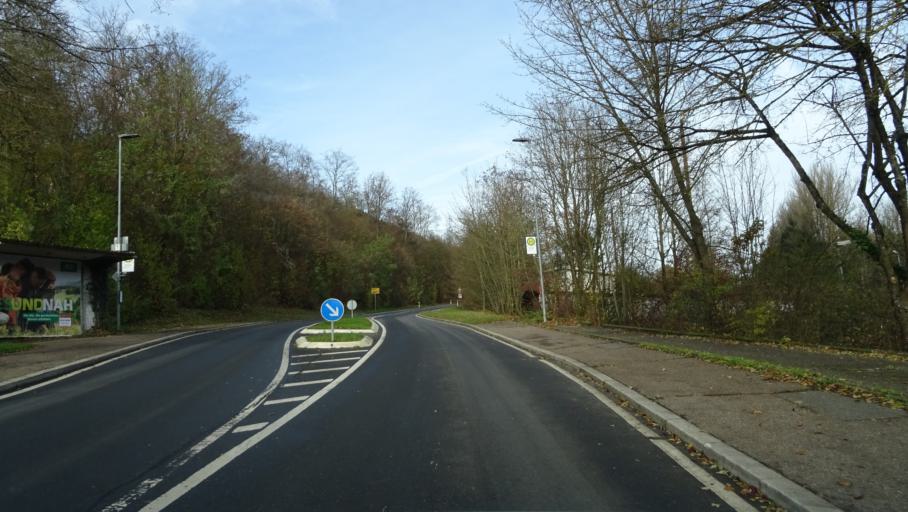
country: DE
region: Baden-Wuerttemberg
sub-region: Karlsruhe Region
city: Mosbach
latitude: 49.3569
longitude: 9.1283
